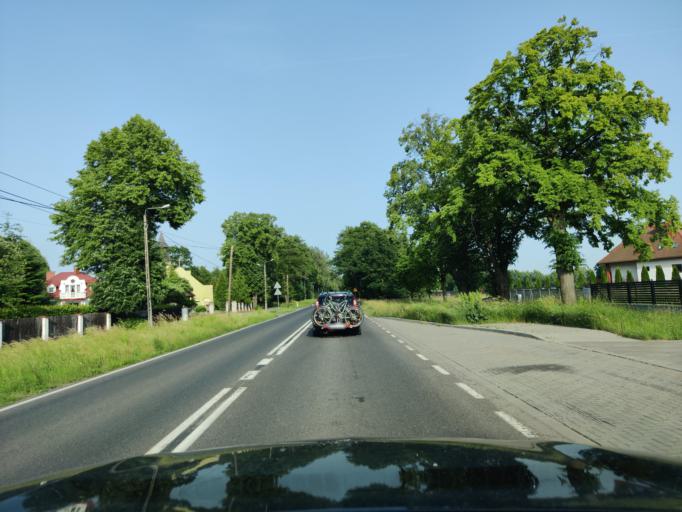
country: PL
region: Masovian Voivodeship
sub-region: Powiat wegrowski
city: Lochow
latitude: 52.5506
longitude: 21.6217
